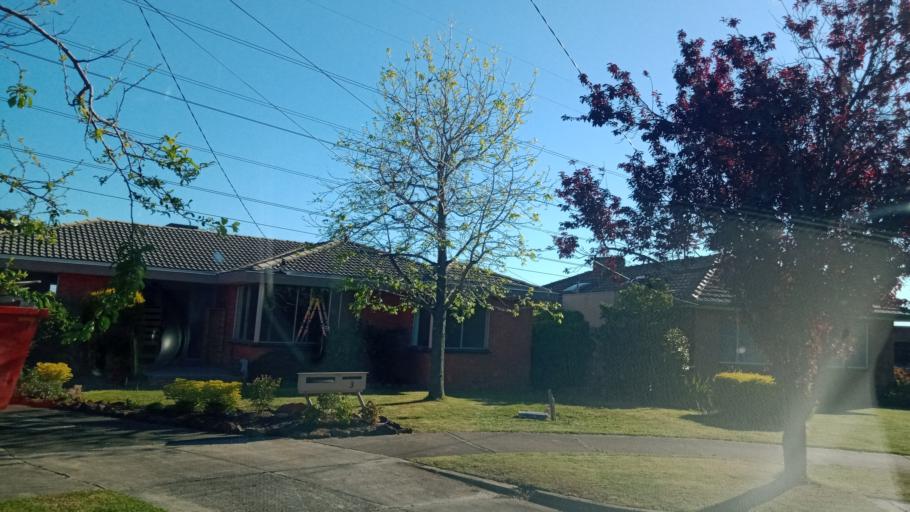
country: AU
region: Victoria
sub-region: Greater Dandenong
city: Springvale
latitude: -37.9270
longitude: 145.1708
